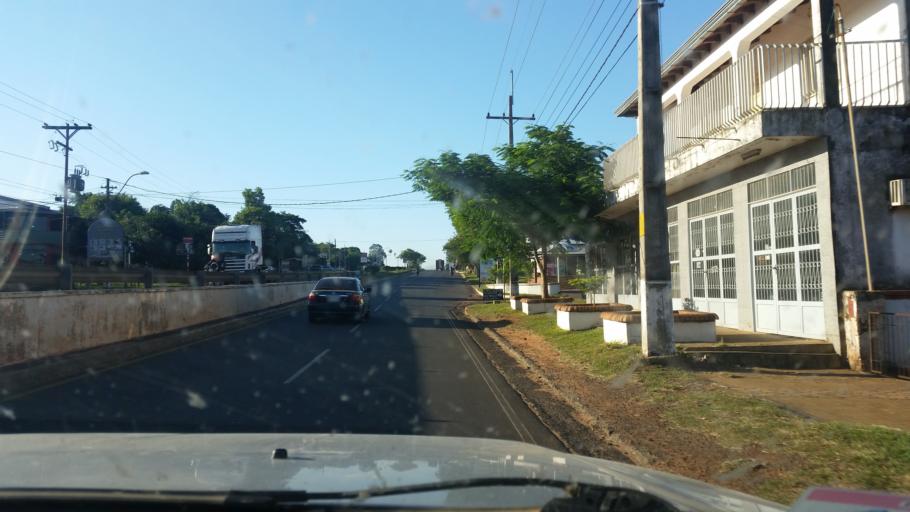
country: PY
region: Misiones
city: Santa Maria
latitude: -26.8829
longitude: -57.0318
